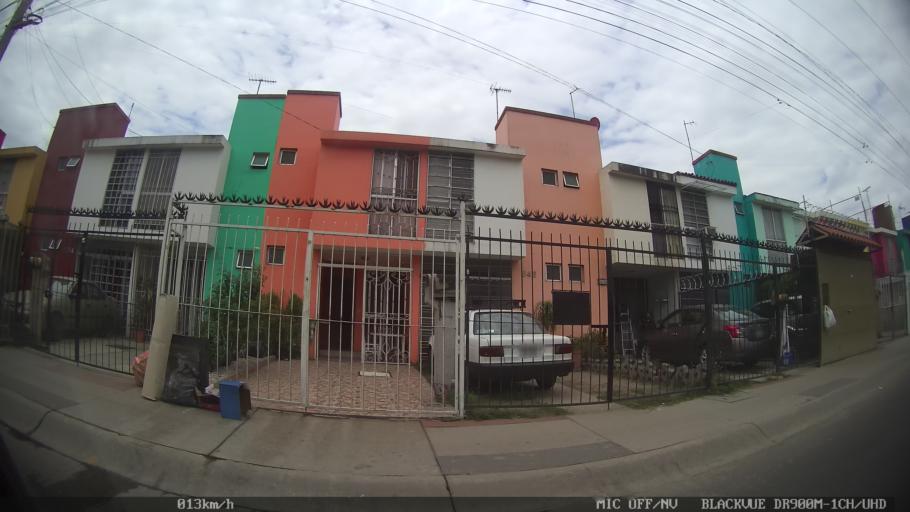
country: MX
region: Jalisco
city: Tlaquepaque
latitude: 20.6451
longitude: -103.2732
